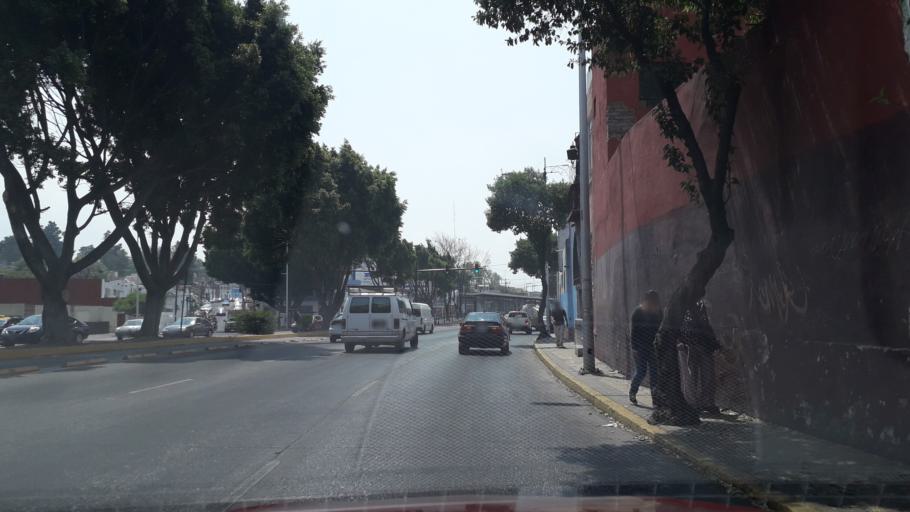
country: MX
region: Puebla
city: Puebla
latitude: 19.0509
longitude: -98.1901
